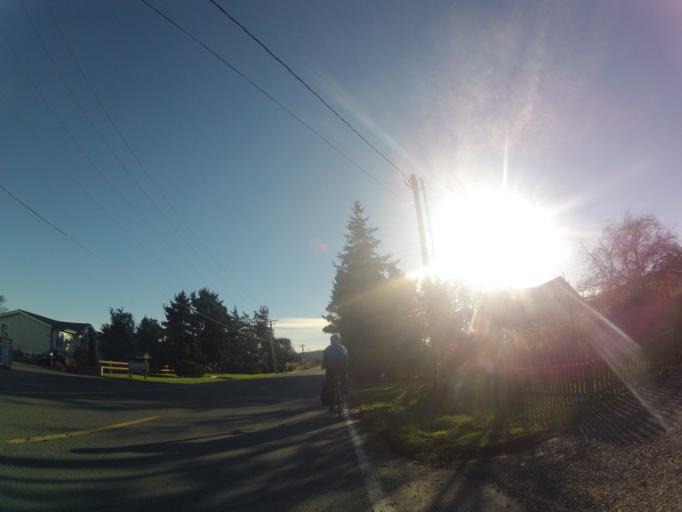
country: US
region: Washington
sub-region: Island County
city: Coupeville
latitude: 48.2049
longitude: -122.6862
